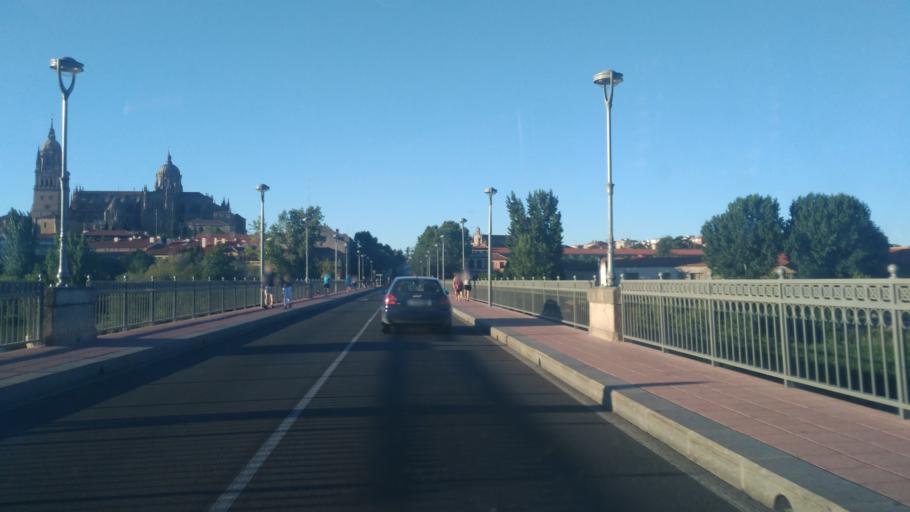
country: ES
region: Castille and Leon
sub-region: Provincia de Salamanca
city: Salamanca
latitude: 40.9553
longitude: -5.6665
